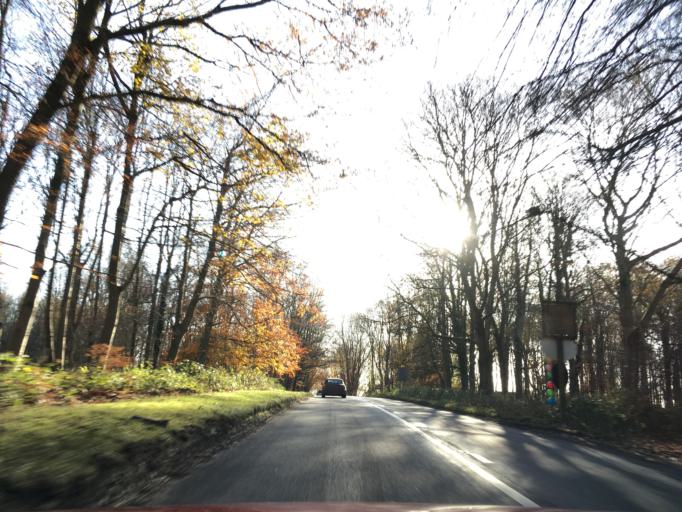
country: GB
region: England
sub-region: Wiltshire
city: Burbage
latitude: 51.3799
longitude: -1.6878
